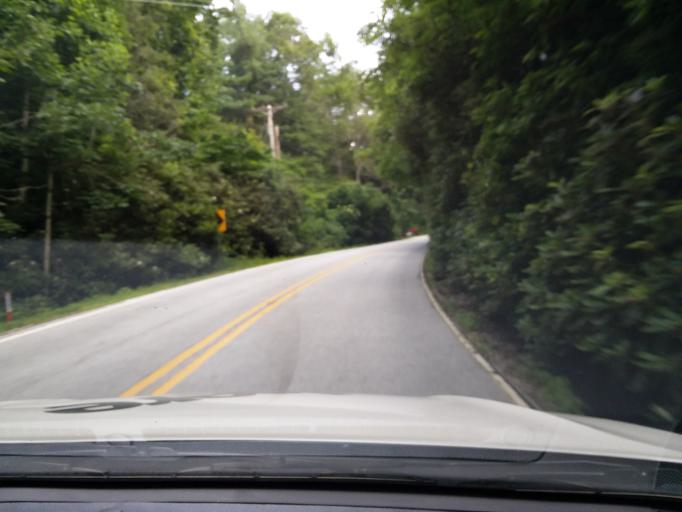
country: US
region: Georgia
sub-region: Rabun County
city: Mountain City
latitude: 35.0372
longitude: -83.2621
